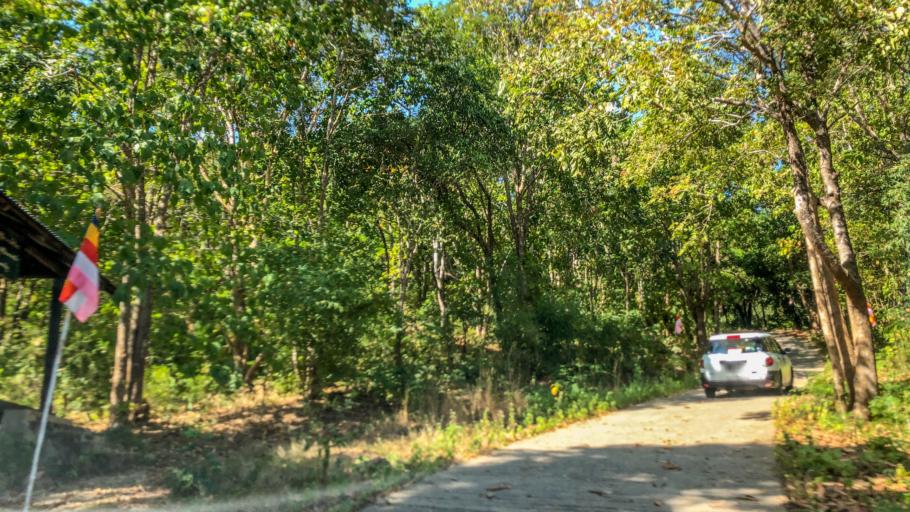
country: MM
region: Magway
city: Magway
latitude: 19.7611
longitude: 94.9389
